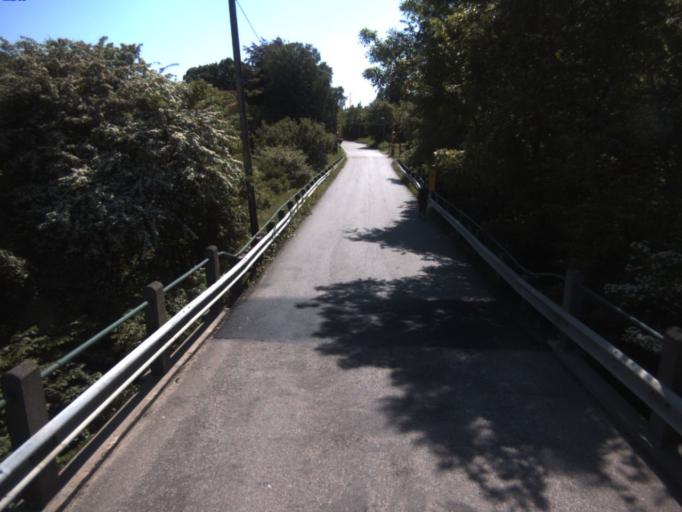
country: SE
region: Skane
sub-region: Helsingborg
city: Rydeback
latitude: 55.9999
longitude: 12.7631
